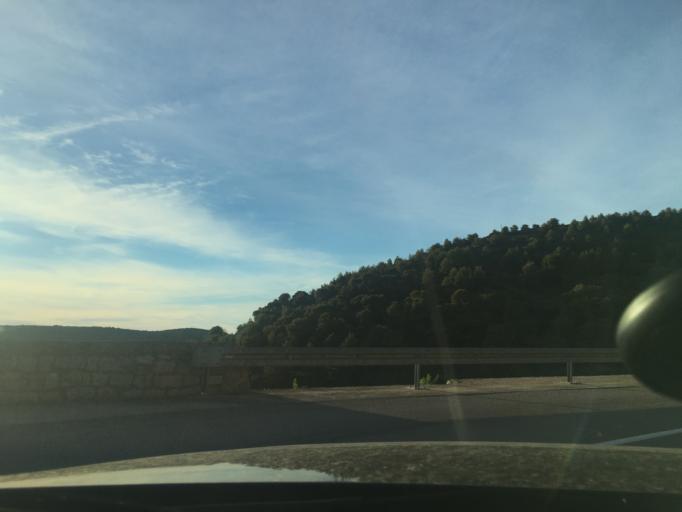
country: HR
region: Splitsko-Dalmatinska
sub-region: Grad Vis
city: Vis
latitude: 43.0570
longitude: 16.2042
